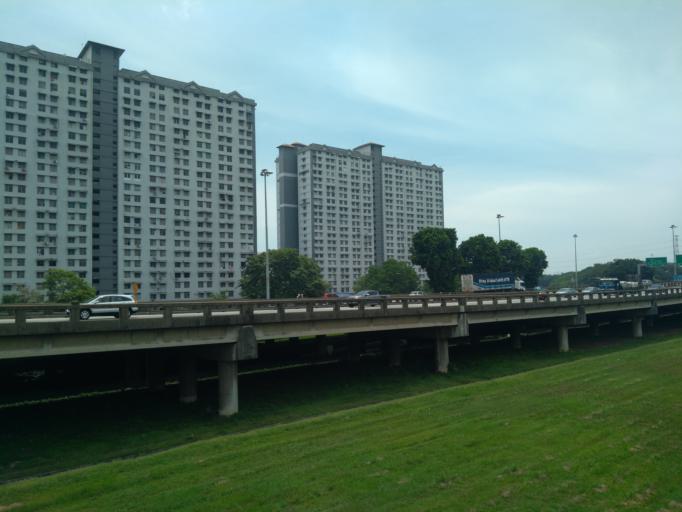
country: MY
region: Penang
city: Perai
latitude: 5.3742
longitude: 100.4022
